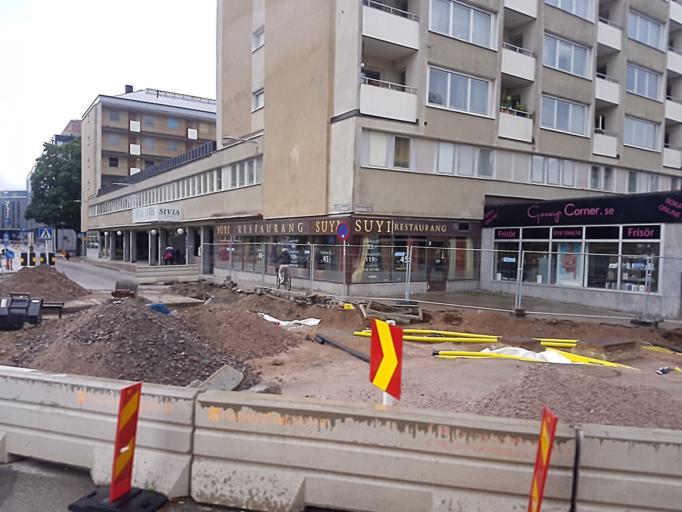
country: SE
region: Uppsala
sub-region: Uppsala Kommun
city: Uppsala
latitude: 59.8610
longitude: 17.6448
